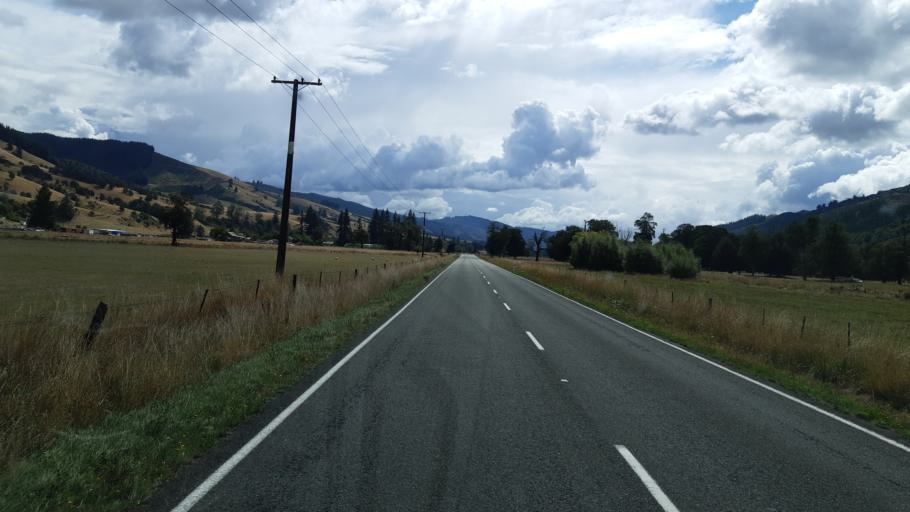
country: NZ
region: Tasman
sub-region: Tasman District
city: Wakefield
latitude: -41.5239
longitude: 172.7957
